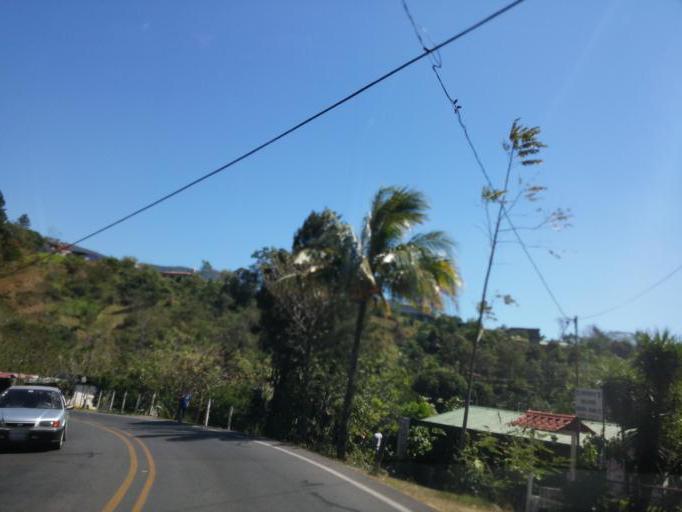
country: CR
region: Heredia
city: Colon
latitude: 9.8969
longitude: -84.2352
